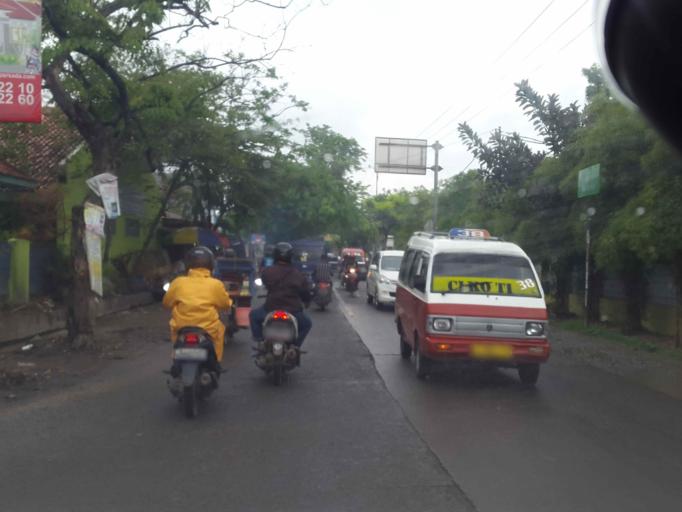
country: ID
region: West Java
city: Cikarang
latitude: -6.2487
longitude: 107.1586
